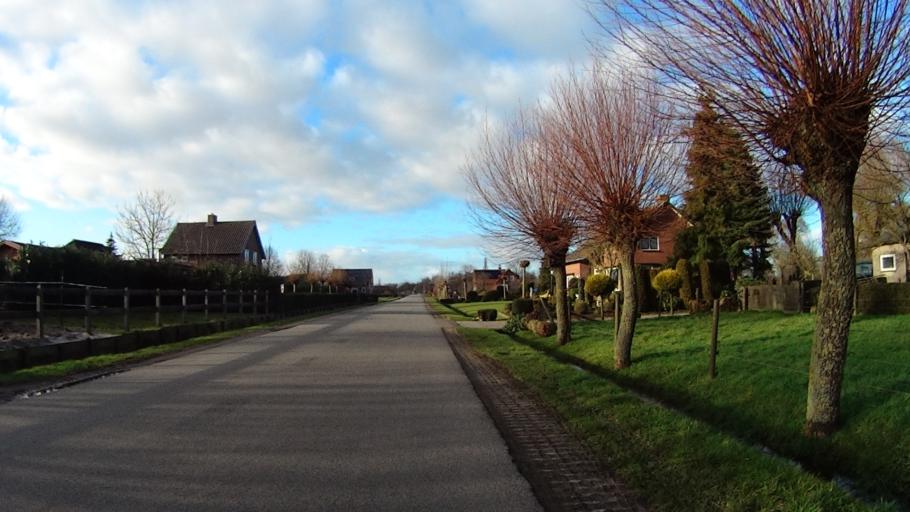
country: NL
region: Gelderland
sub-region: Gemeente Barneveld
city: Zwartebroek
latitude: 52.1838
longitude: 5.4984
